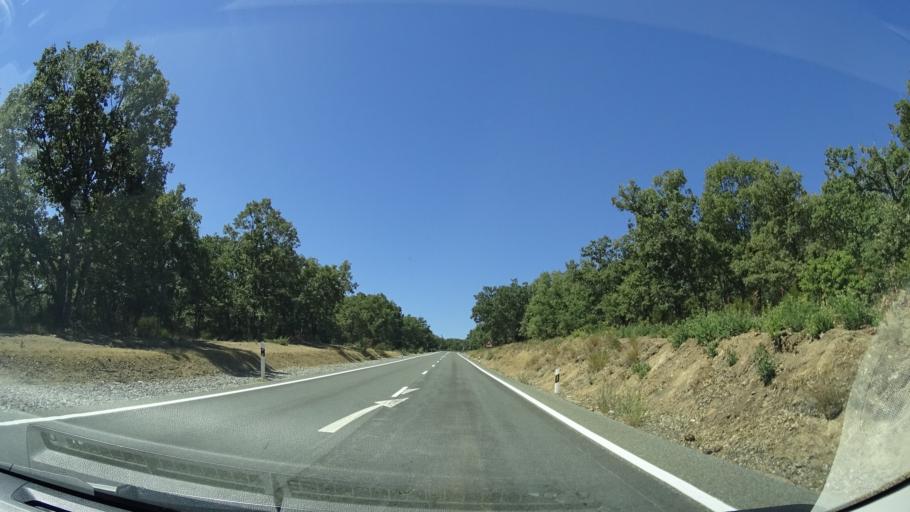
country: ES
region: Castille and Leon
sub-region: Provincia de Avila
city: Navalperal de Pinares
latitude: 40.5900
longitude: -4.4714
